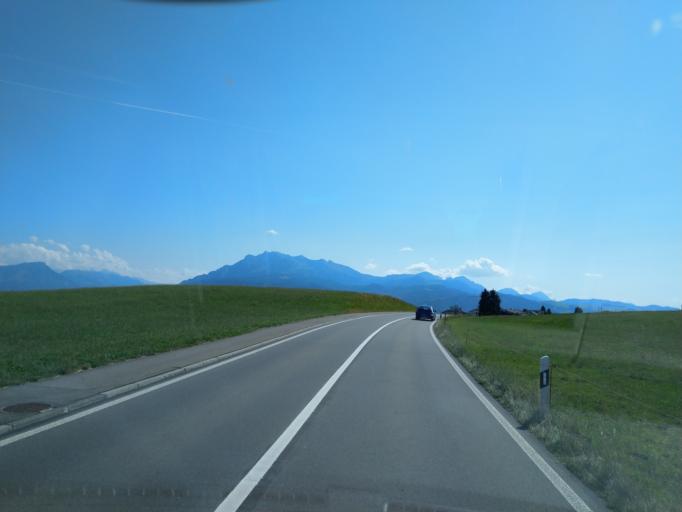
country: CH
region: Lucerne
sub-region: Hochdorf District
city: Emmen
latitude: 47.1047
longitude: 8.2878
